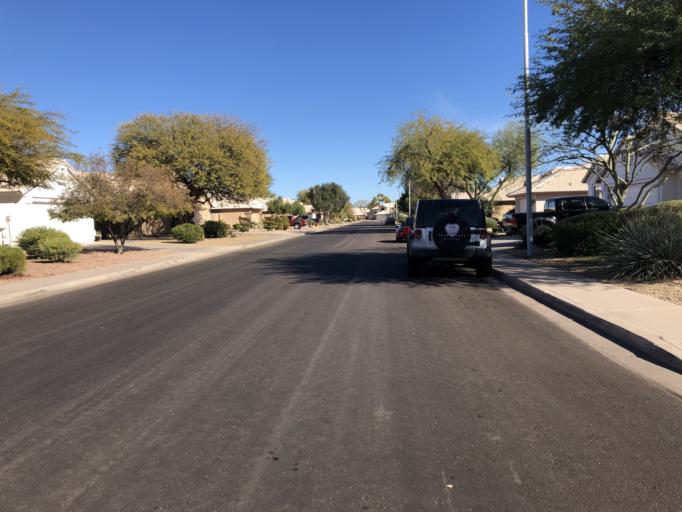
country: US
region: Arizona
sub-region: Maricopa County
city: San Carlos
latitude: 33.3139
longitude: -111.9153
